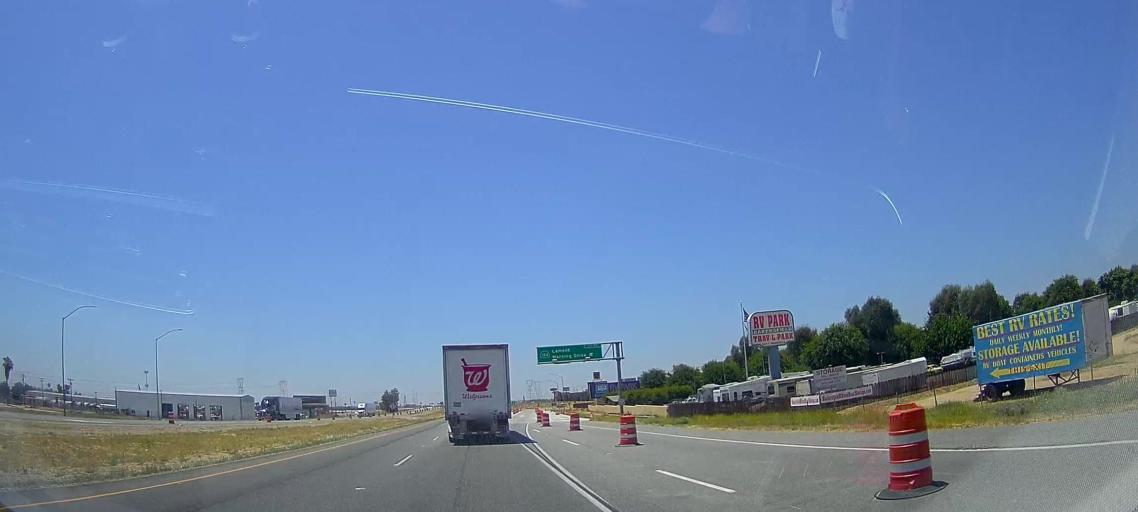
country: US
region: California
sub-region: Kern County
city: Lamont
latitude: 35.3520
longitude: -118.9078
